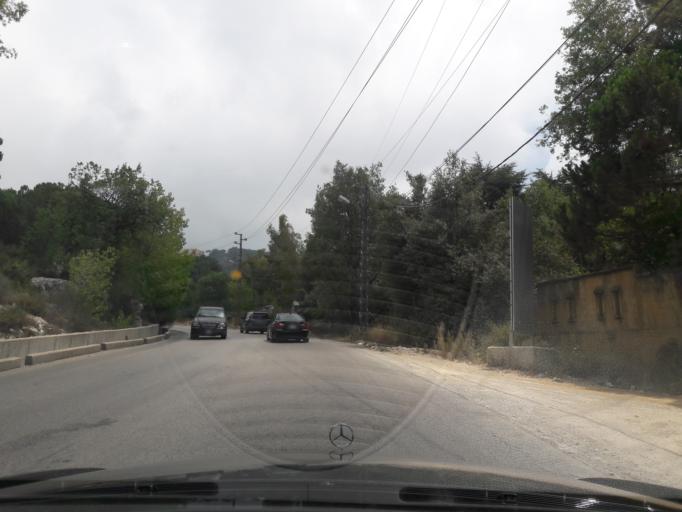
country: LB
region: Mont-Liban
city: Djounie
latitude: 33.9145
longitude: 35.6869
